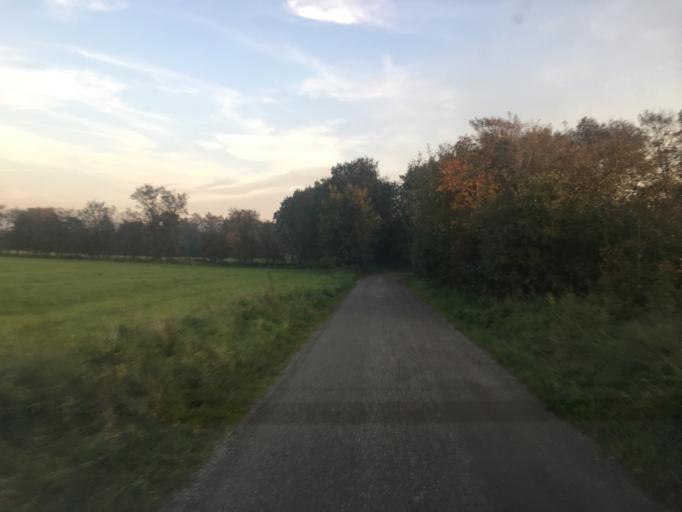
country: DE
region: Schleswig-Holstein
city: Bramstedtlund
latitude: 54.9871
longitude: 9.0922
